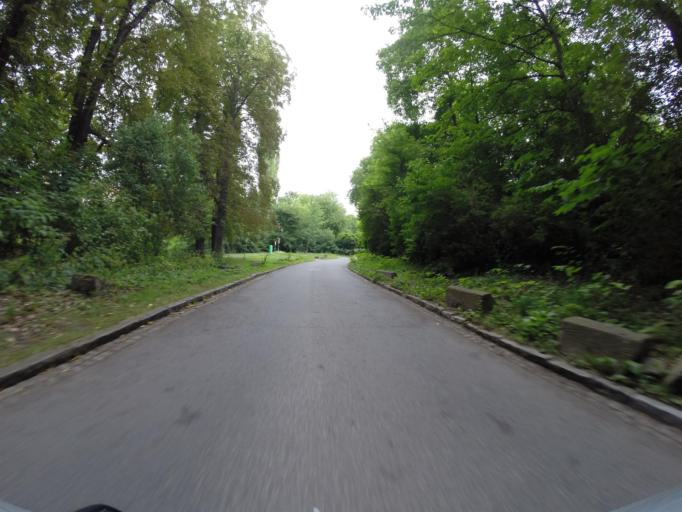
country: DE
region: Thuringia
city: Weimar
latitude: 50.9803
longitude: 11.3348
